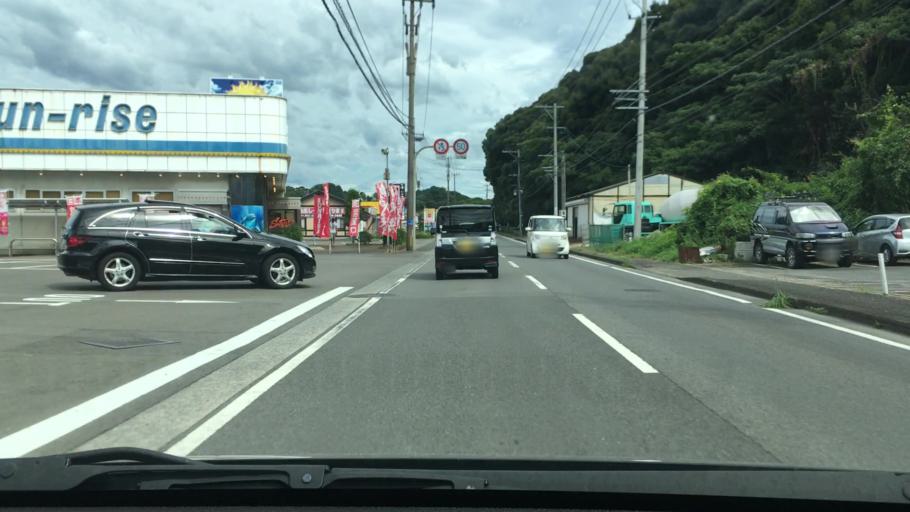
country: JP
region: Nagasaki
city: Togitsu
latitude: 32.8882
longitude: 129.7874
